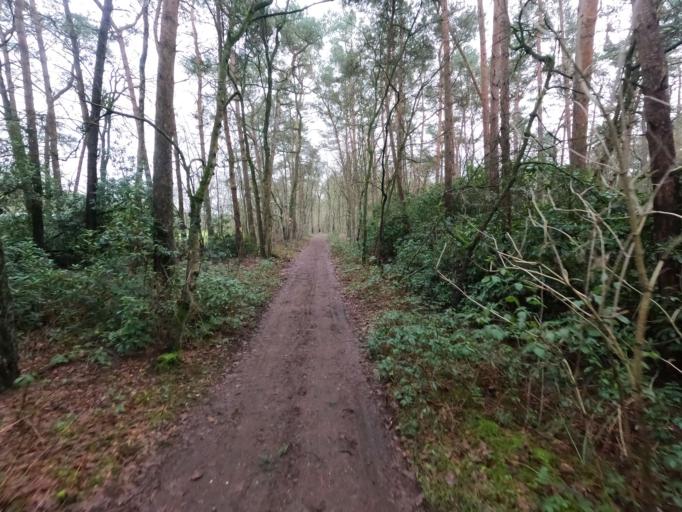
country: BE
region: Flanders
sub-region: Provincie Antwerpen
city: Schilde
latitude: 51.2983
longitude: 4.6051
